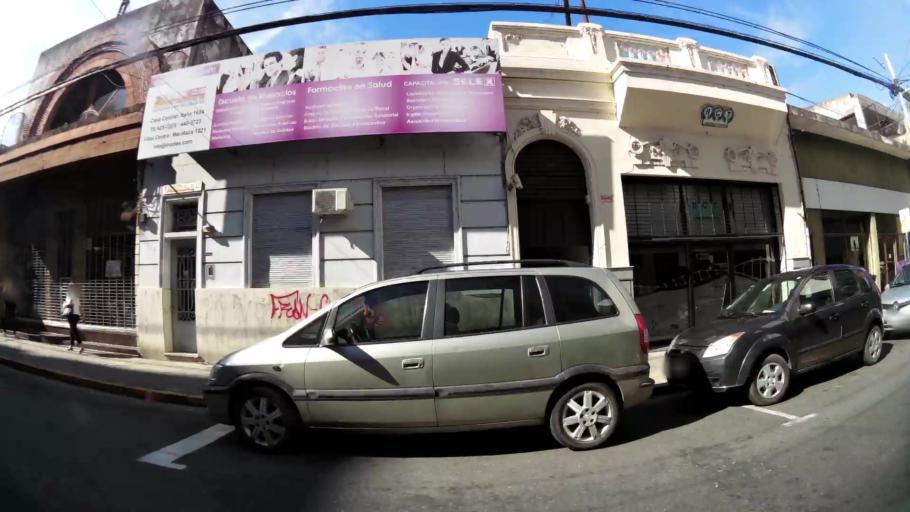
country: AR
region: Santa Fe
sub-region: Departamento de Rosario
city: Rosario
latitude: -32.9514
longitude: -60.6415
